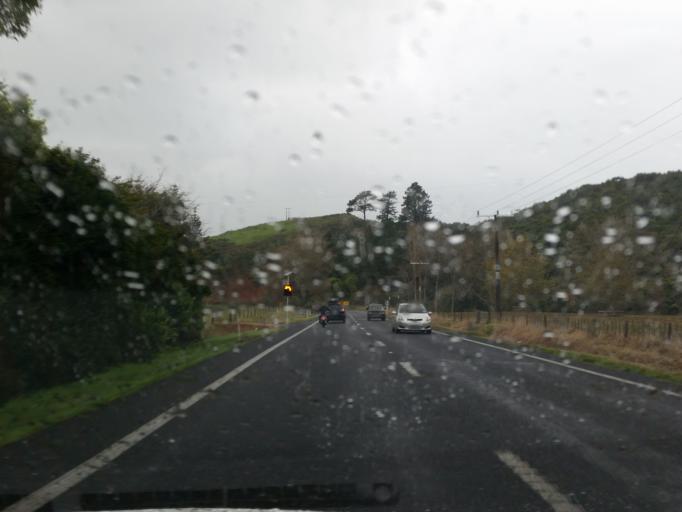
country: NZ
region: Waikato
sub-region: Hauraki District
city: Waihi
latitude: -37.4193
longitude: 175.7504
